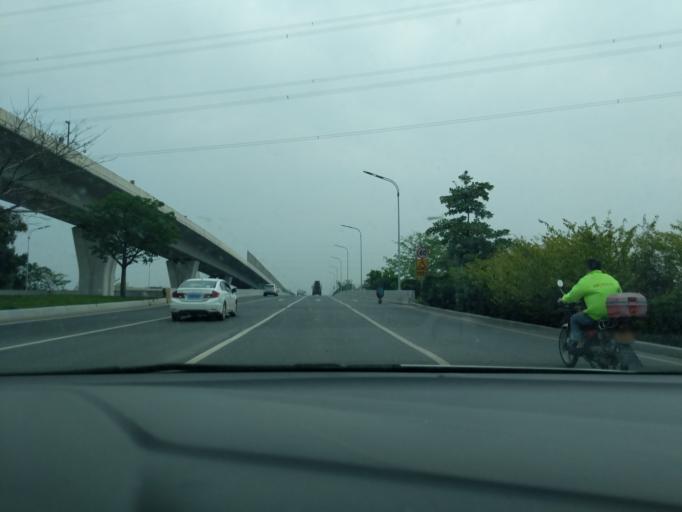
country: CN
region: Guangdong
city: Huangge
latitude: 22.8557
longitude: 113.4894
